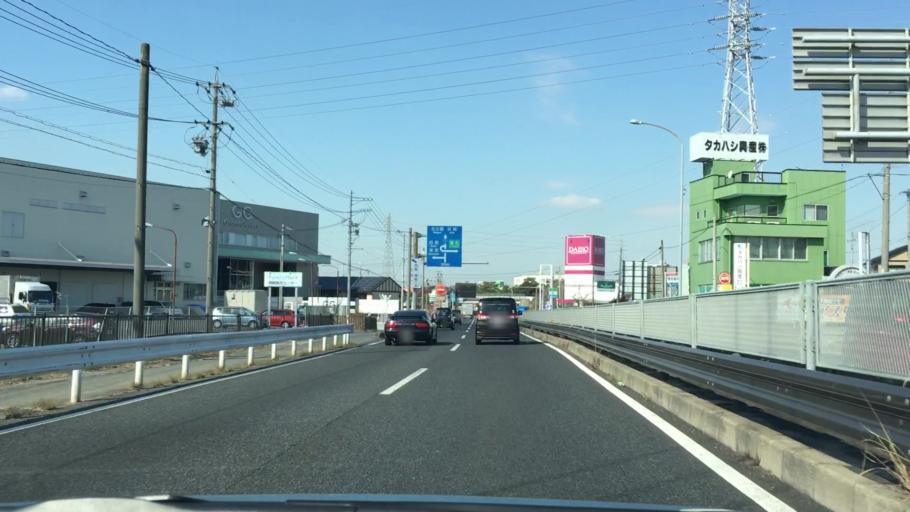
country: JP
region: Aichi
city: Okazaki
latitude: 34.9423
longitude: 137.1916
